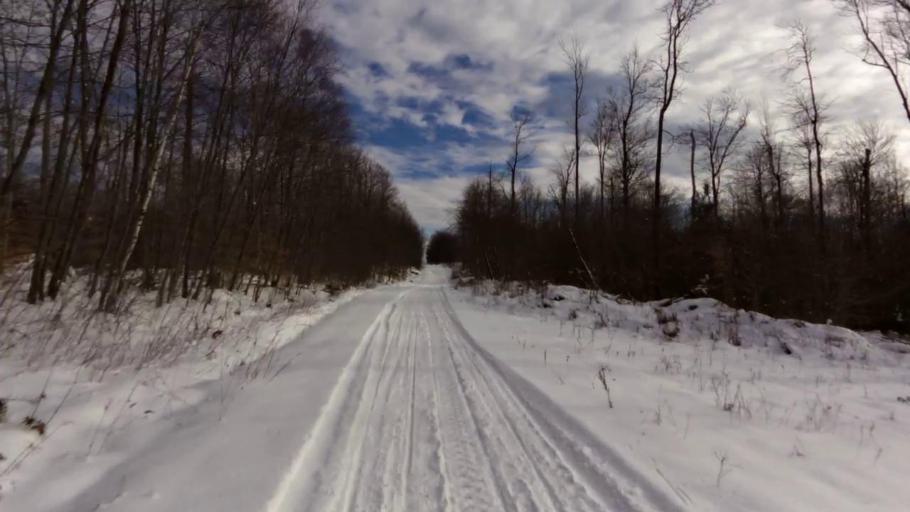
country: US
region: Pennsylvania
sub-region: McKean County
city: Foster Brook
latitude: 42.0158
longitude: -78.5481
